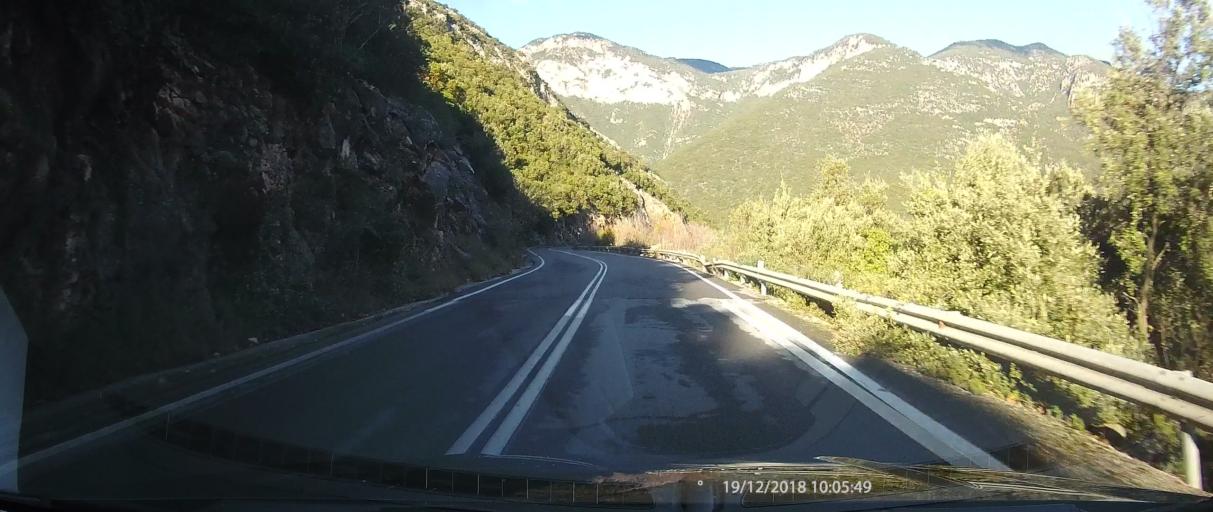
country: GR
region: Peloponnese
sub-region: Nomos Messinias
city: Paralia Vergas
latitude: 37.1116
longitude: 22.2129
